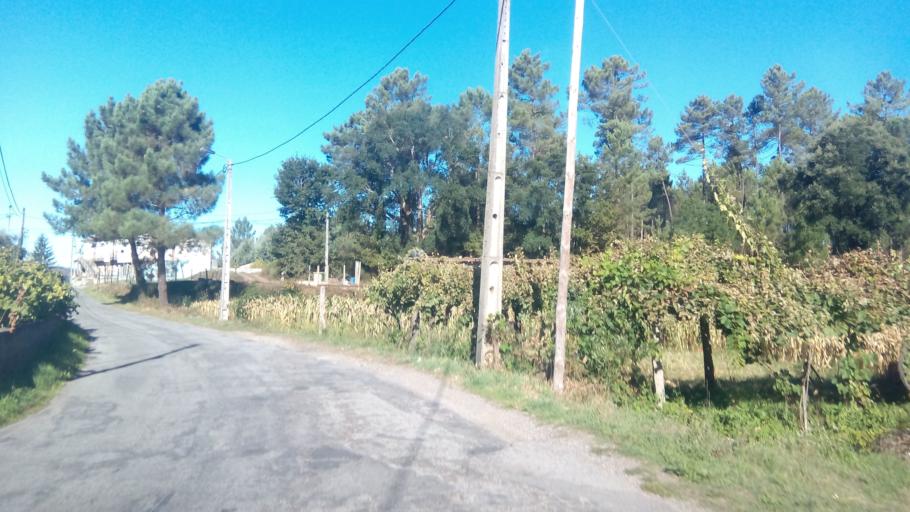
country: PT
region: Porto
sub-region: Paredes
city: Gandra
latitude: 41.1911
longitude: -8.4458
